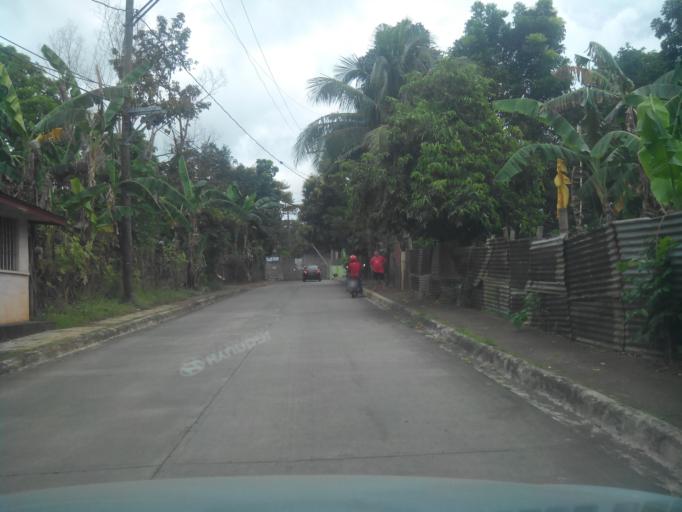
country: PH
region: Calabarzon
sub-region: Province of Rizal
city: Teresa
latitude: 14.6011
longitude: 121.1818
